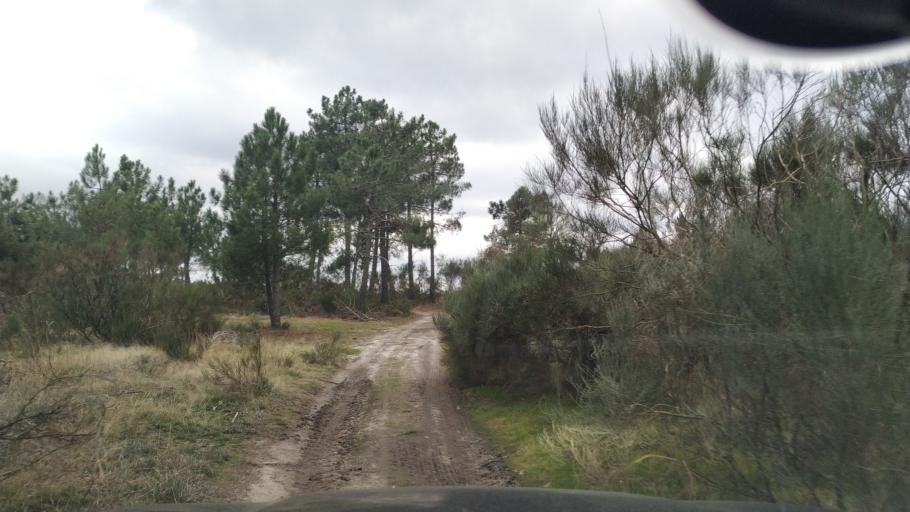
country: PT
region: Vila Real
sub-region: Sabrosa
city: Sabrosa
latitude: 41.3352
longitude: -7.6305
